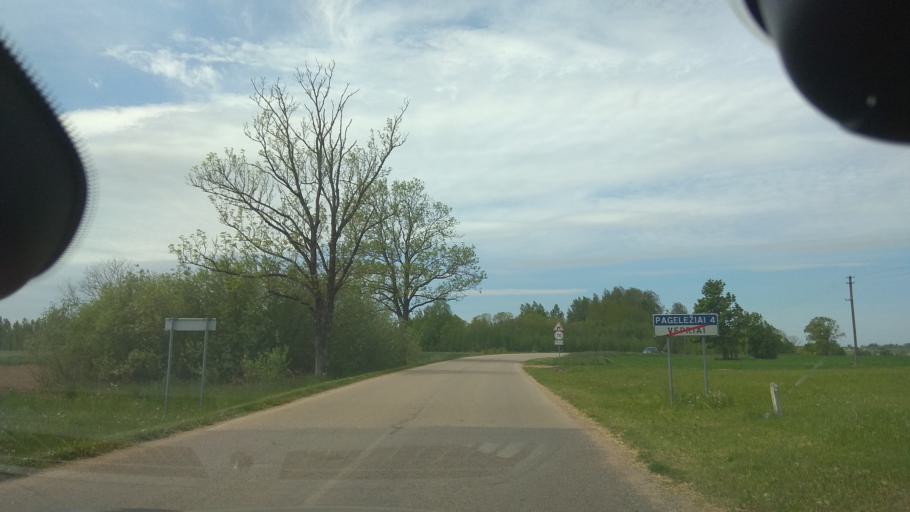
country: LT
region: Vilnius County
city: Ukmerge
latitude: 55.1486
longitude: 24.5614
